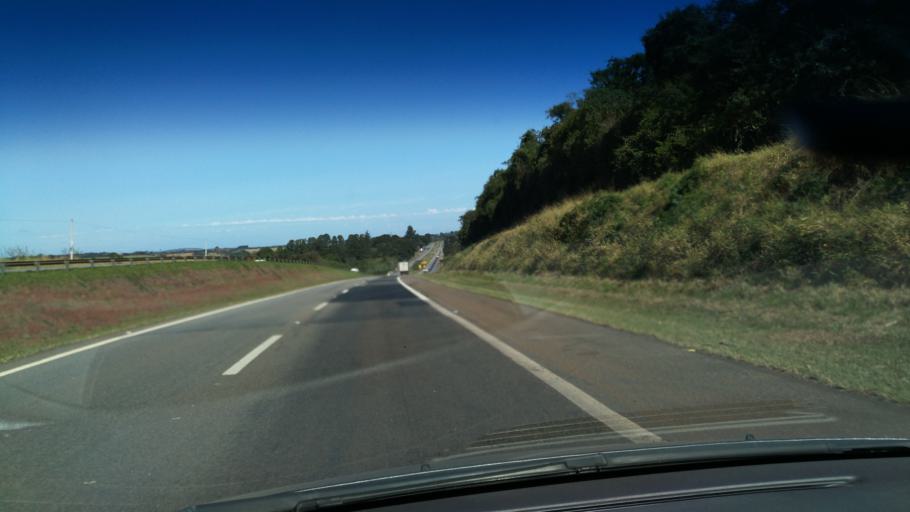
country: BR
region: Sao Paulo
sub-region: Santo Antonio De Posse
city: Santo Antonio de Posse
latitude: -22.5533
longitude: -46.9989
